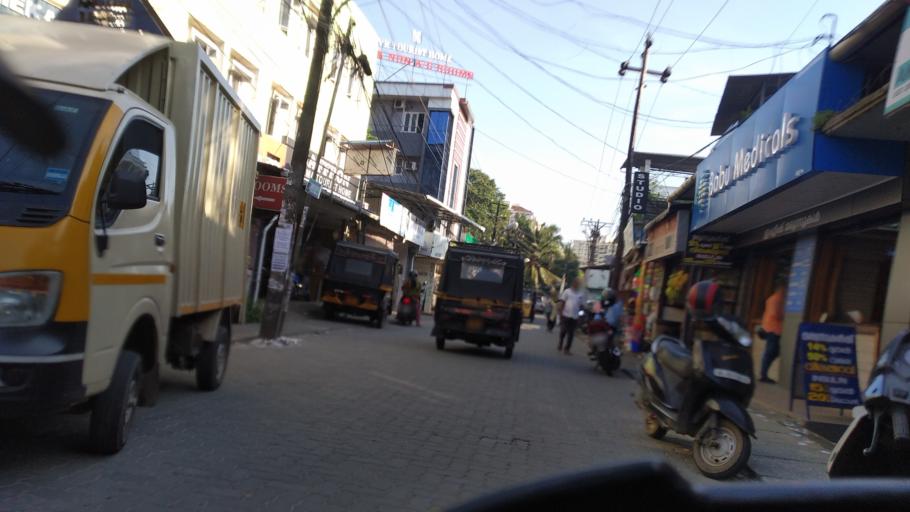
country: IN
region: Kerala
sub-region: Ernakulam
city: Cochin
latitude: 9.9904
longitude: 76.2879
